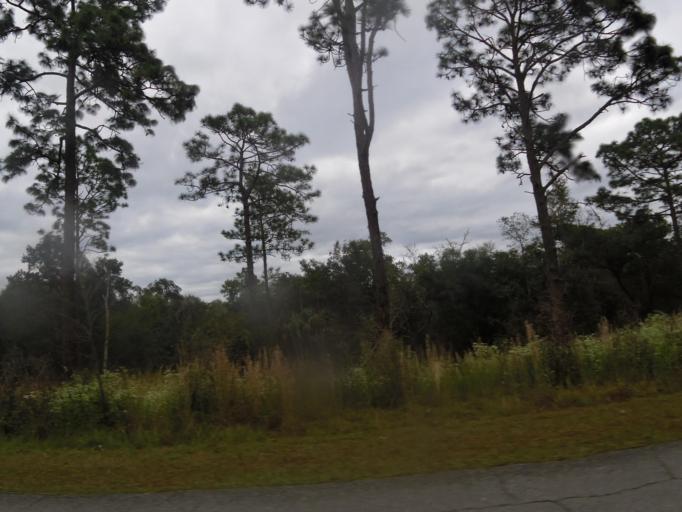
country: US
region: Florida
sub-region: Clay County
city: Keystone Heights
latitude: 29.8364
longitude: -81.9528
